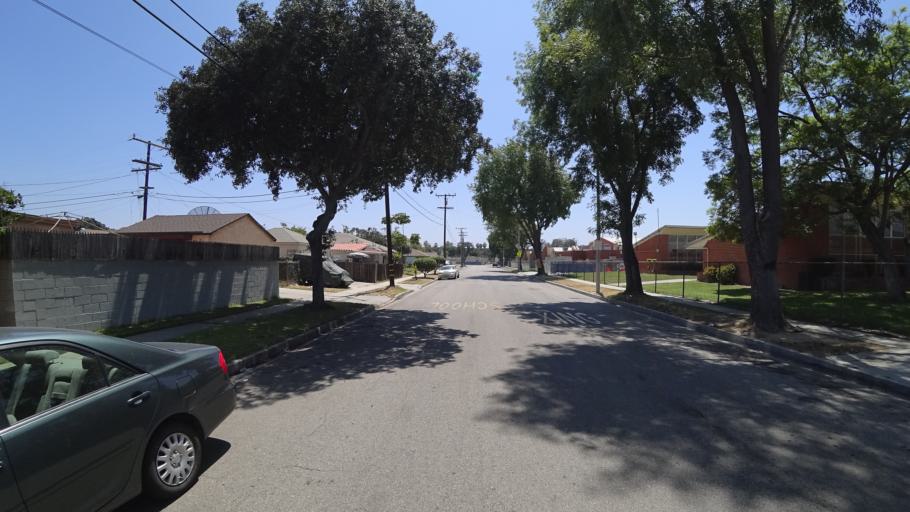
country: US
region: California
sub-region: Los Angeles County
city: Lennox
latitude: 33.9275
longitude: -118.3320
